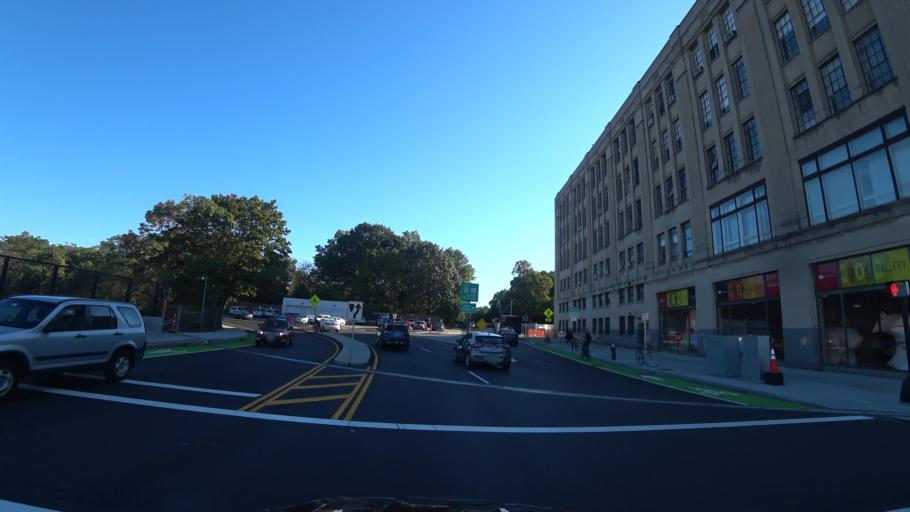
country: US
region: Massachusetts
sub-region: Norfolk County
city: Brookline
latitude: 42.3504
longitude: -71.1110
